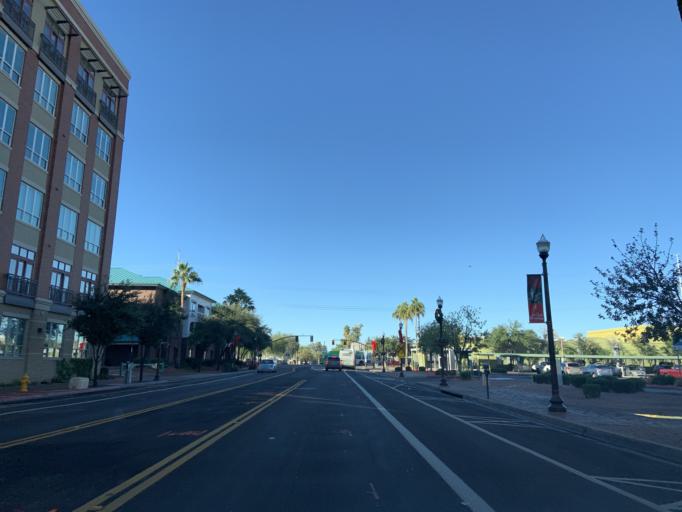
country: US
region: Arizona
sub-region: Maricopa County
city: Tempe Junction
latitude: 33.4255
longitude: -111.9419
